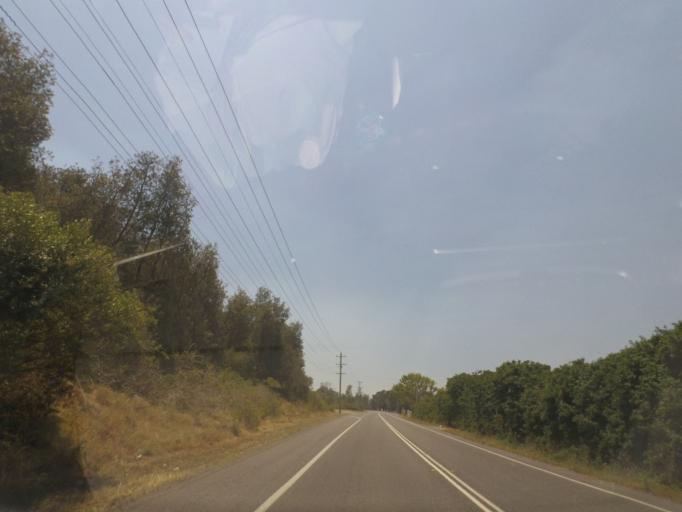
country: AU
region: New South Wales
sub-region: Port Stephens Shire
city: Medowie
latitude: -32.8071
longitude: 151.8714
